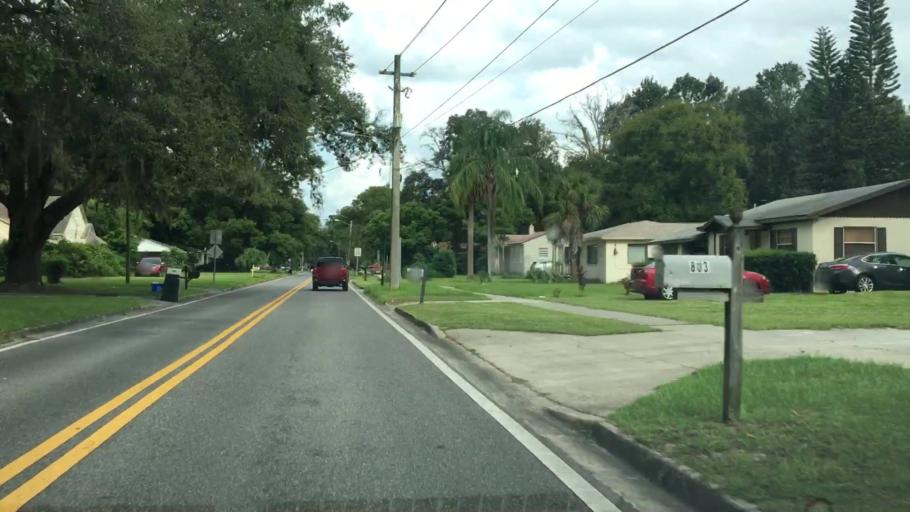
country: US
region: Florida
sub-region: Seminole County
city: Sanford
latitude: 28.7940
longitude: -81.2603
